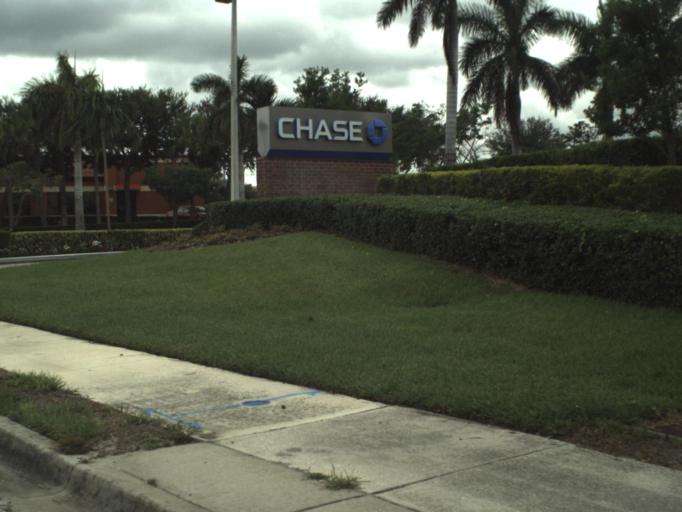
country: US
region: Florida
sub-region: Palm Beach County
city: Jupiter
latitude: 26.9682
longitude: -80.0867
